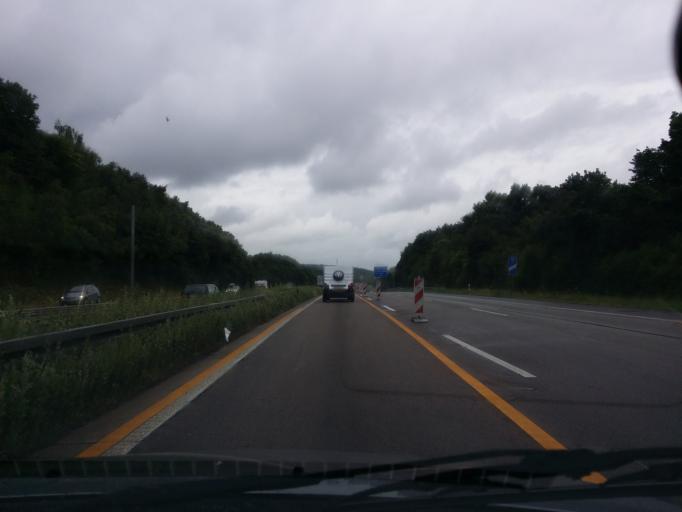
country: DE
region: Hesse
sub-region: Regierungsbezirk Darmstadt
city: Idstein
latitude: 50.2065
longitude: 8.2522
